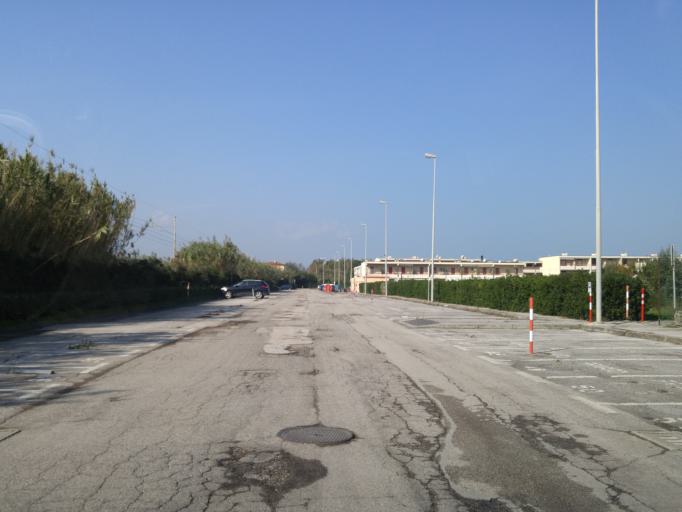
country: IT
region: The Marches
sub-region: Provincia di Pesaro e Urbino
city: Fano
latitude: 43.8301
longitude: 13.0515
